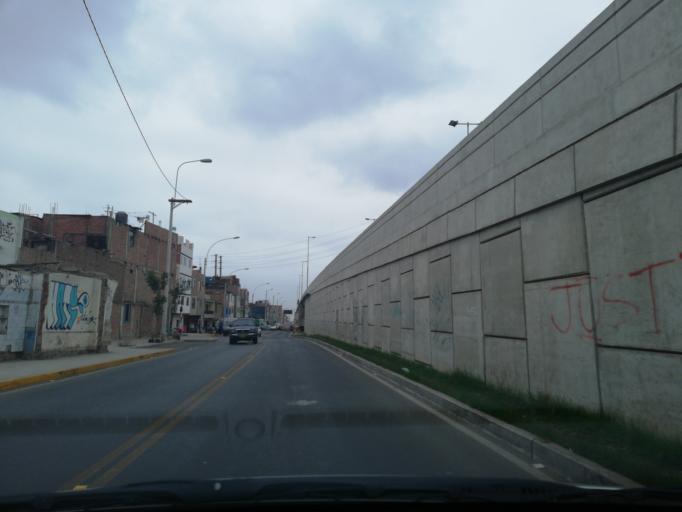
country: PE
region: Lima
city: Lima
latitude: -12.0356
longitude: -77.0643
